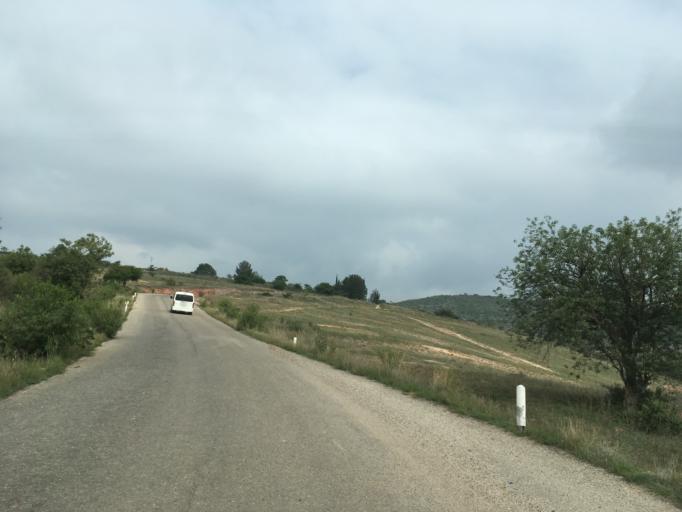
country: MX
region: Oaxaca
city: Magdalena Jaltepec
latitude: 17.3154
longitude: -97.2330
